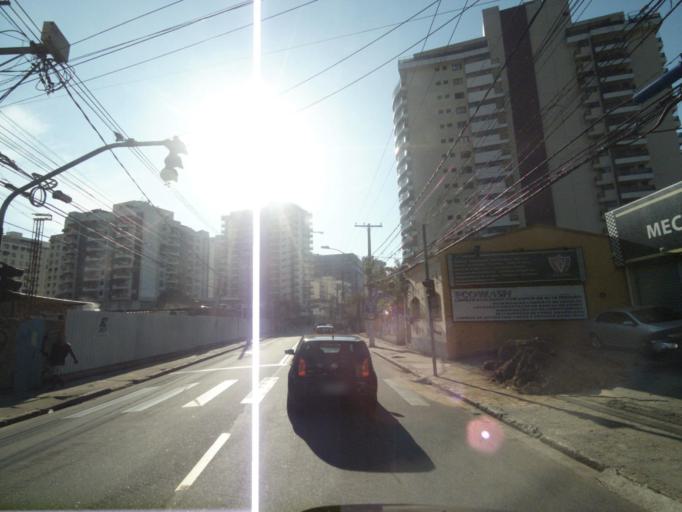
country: BR
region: Rio de Janeiro
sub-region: Niteroi
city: Niteroi
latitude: -22.9029
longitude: -43.0973
